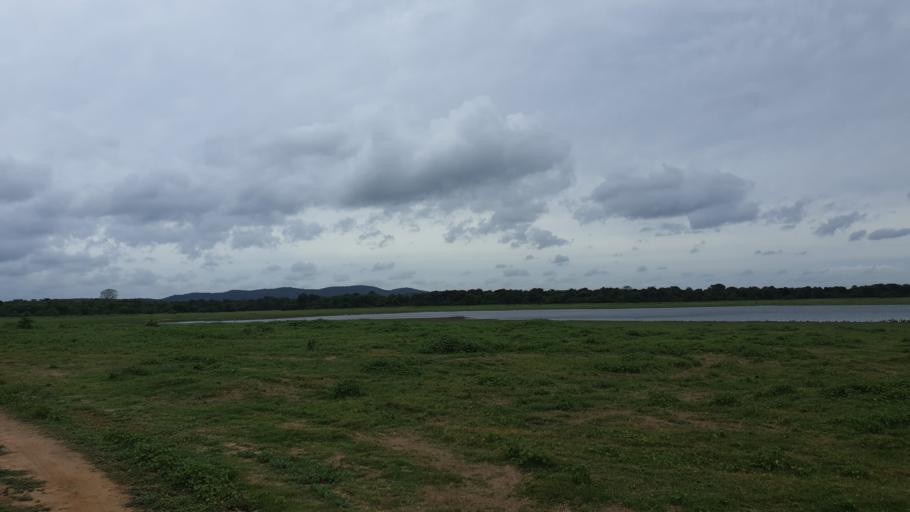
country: LK
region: North Central
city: Polonnaruwa
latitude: 8.1333
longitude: 80.9102
